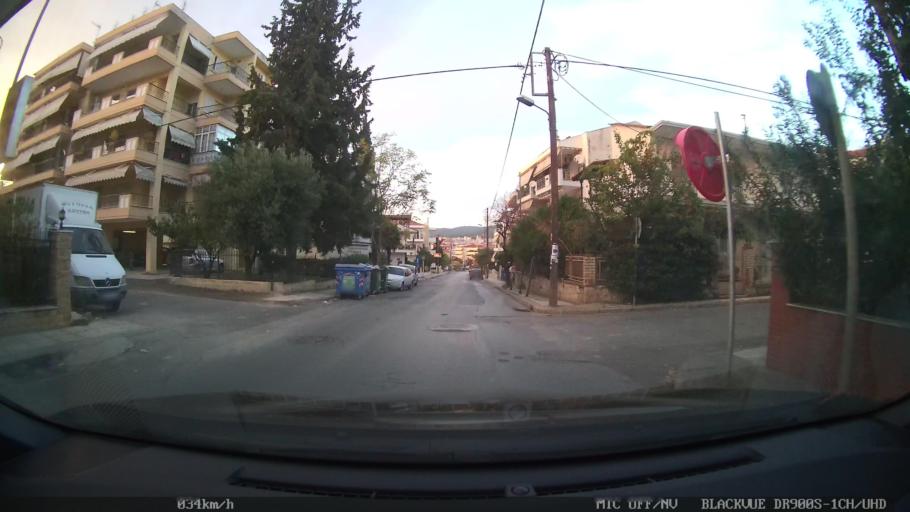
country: GR
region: Central Macedonia
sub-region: Nomos Thessalonikis
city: Pylaia
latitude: 40.6025
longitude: 22.9894
